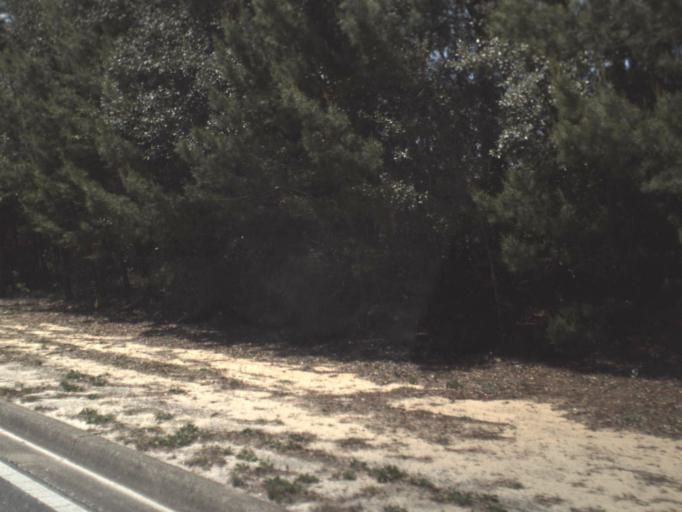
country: US
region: Florida
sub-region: Okaloosa County
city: Niceville
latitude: 30.5287
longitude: -86.4630
